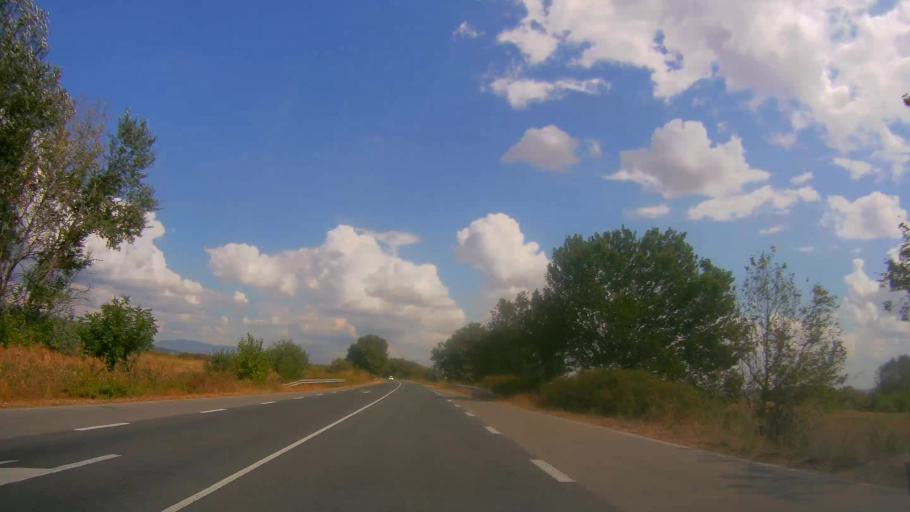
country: BG
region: Sliven
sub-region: Obshtina Sliven
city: Kermen
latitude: 42.6309
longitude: 26.1825
